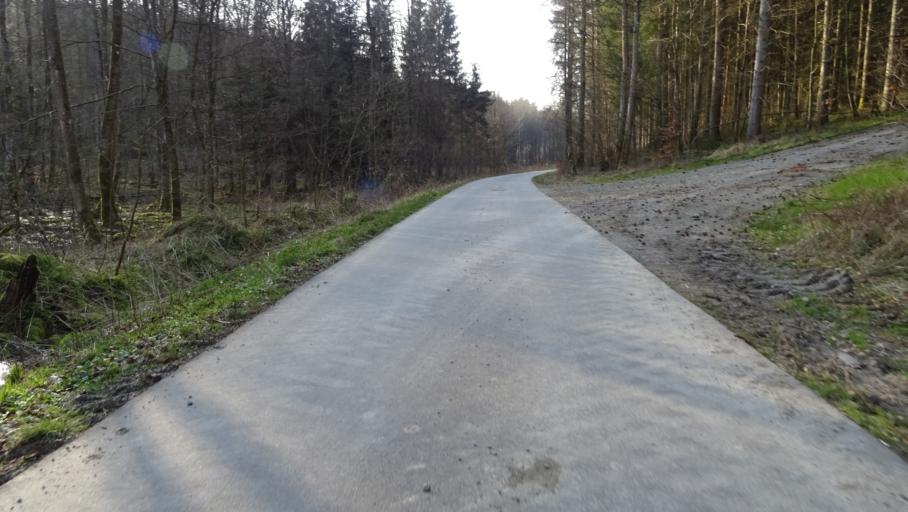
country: DE
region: Baden-Wuerttemberg
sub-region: Regierungsbezirk Stuttgart
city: Roigheim
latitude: 49.3873
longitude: 9.3382
